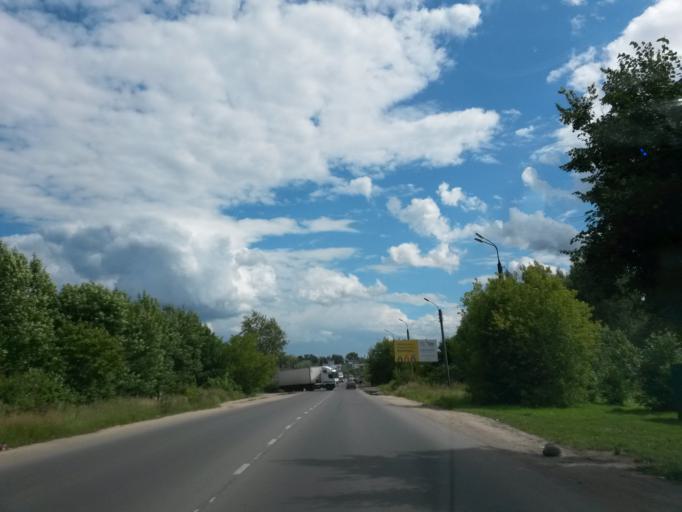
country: RU
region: Ivanovo
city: Novo-Talitsy
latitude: 57.0019
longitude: 40.8944
